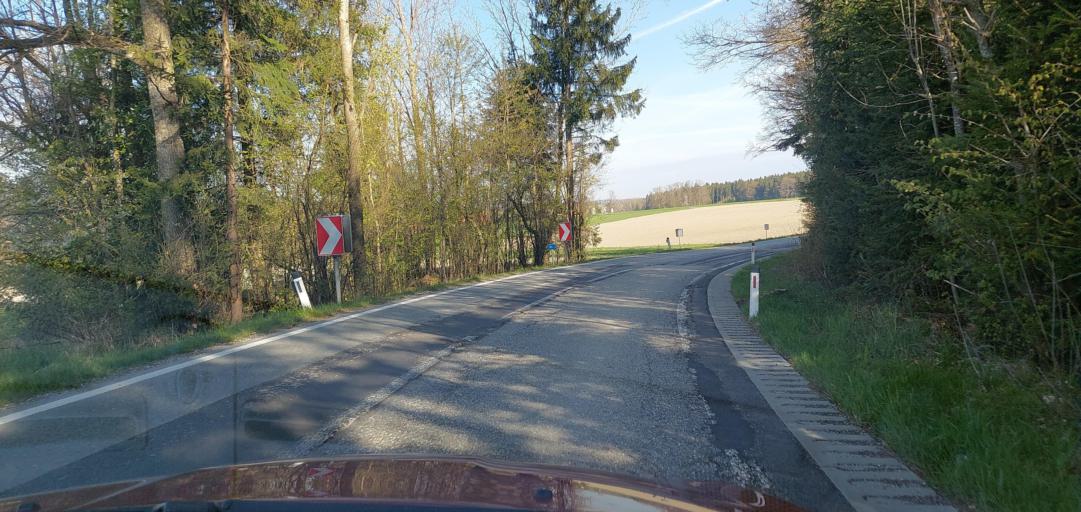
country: AT
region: Upper Austria
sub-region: Politischer Bezirk Ried im Innkreis
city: Ried im Innkreis
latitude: 48.1732
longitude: 13.5530
